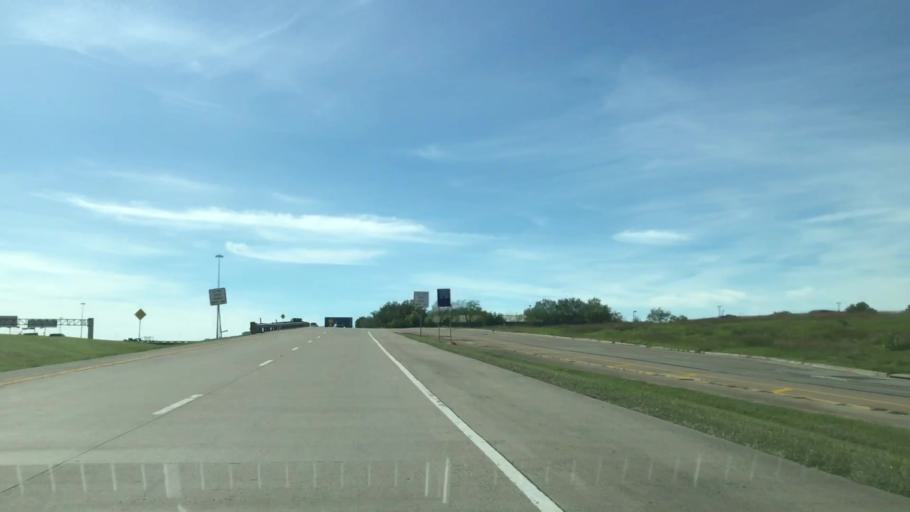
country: US
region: Texas
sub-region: Dallas County
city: Farmers Branch
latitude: 32.9103
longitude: -96.9492
